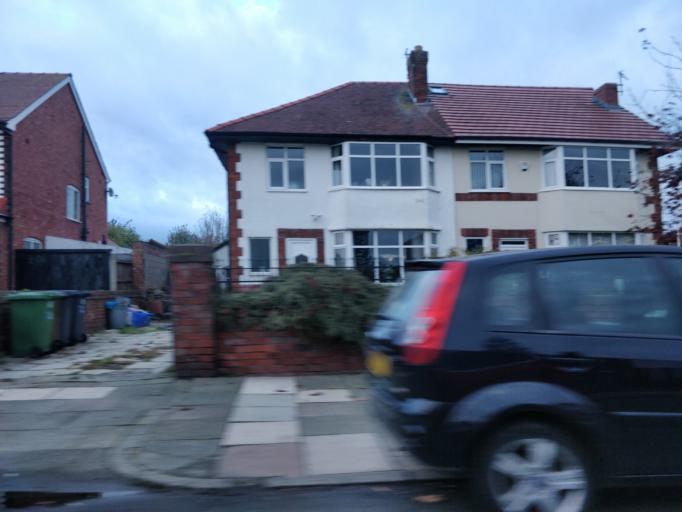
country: GB
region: England
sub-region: Sefton
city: Southport
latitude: 53.6644
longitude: -2.9738
